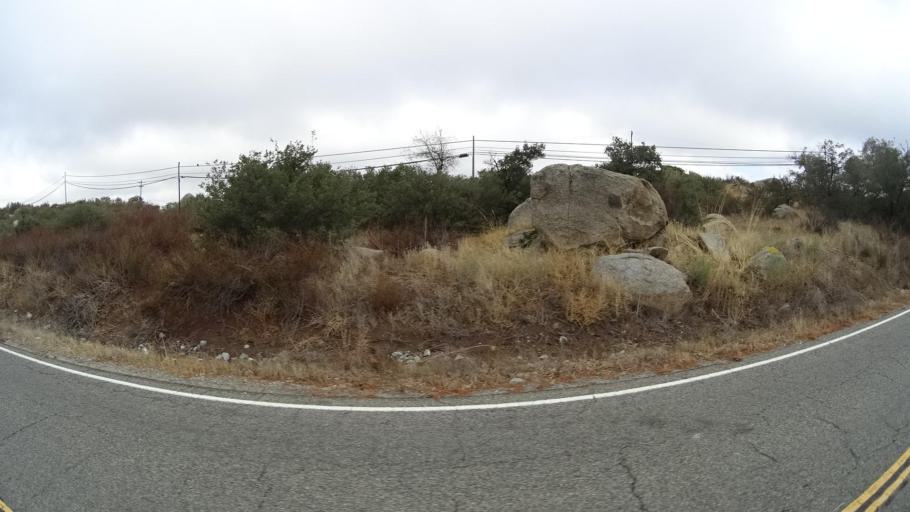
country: MX
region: Baja California
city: Tecate
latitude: 32.5998
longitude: -116.5848
